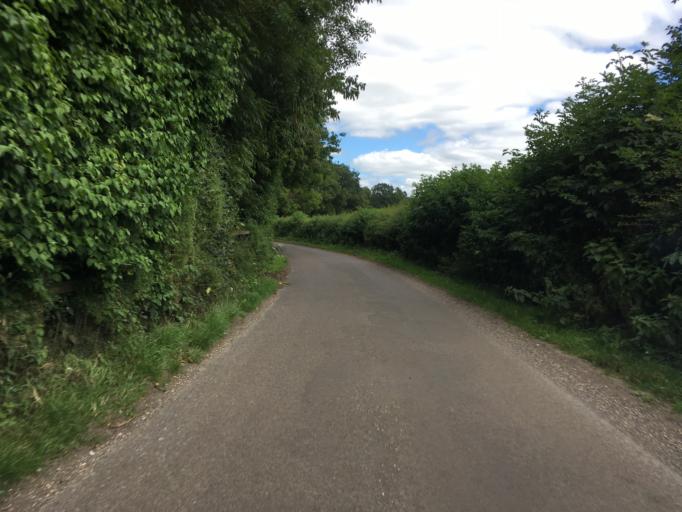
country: GB
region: England
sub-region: Hampshire
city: Highclere
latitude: 51.2779
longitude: -1.4205
